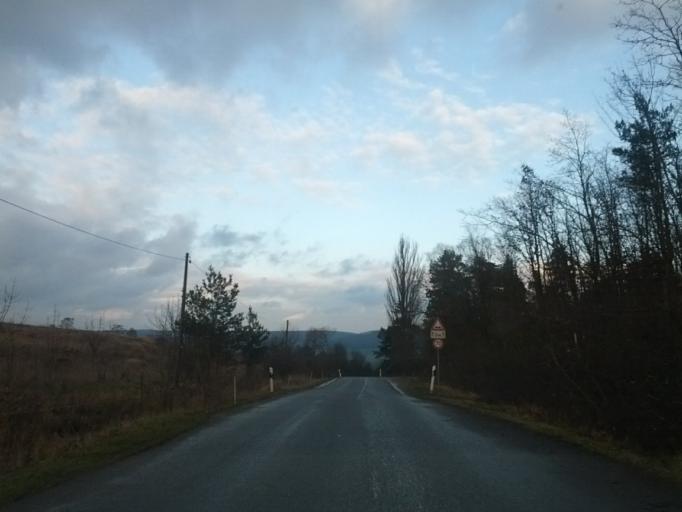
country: DE
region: Thuringia
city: Bischofroda
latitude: 51.0423
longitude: 10.3495
